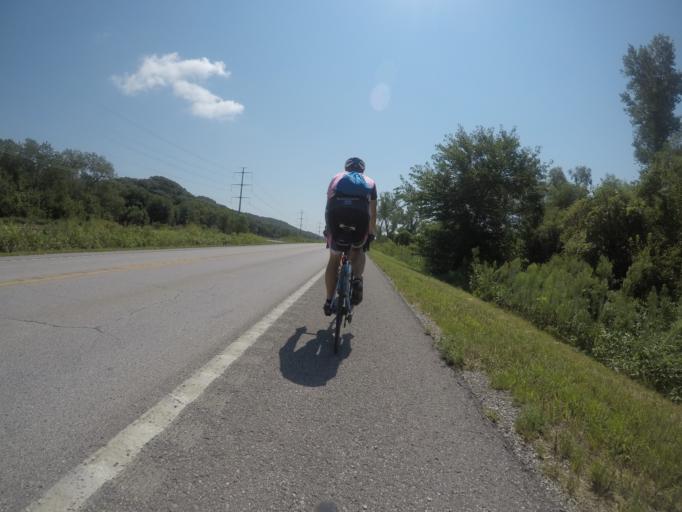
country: US
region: Missouri
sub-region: Platte County
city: Weston
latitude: 39.4547
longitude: -94.9629
